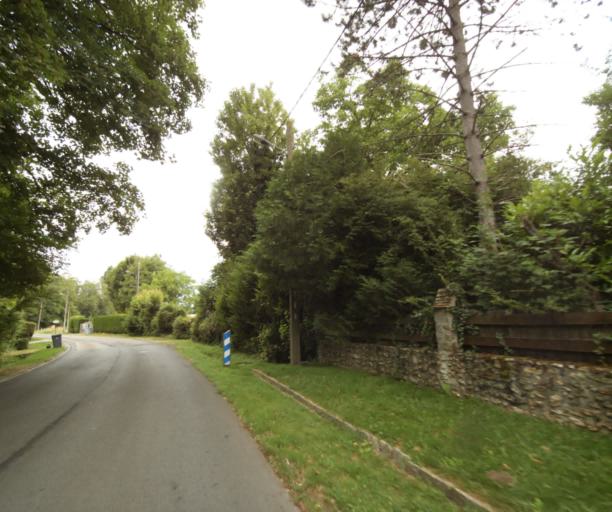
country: FR
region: Ile-de-France
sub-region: Departement de Seine-et-Marne
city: Cely
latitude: 48.4515
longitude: 2.5459
